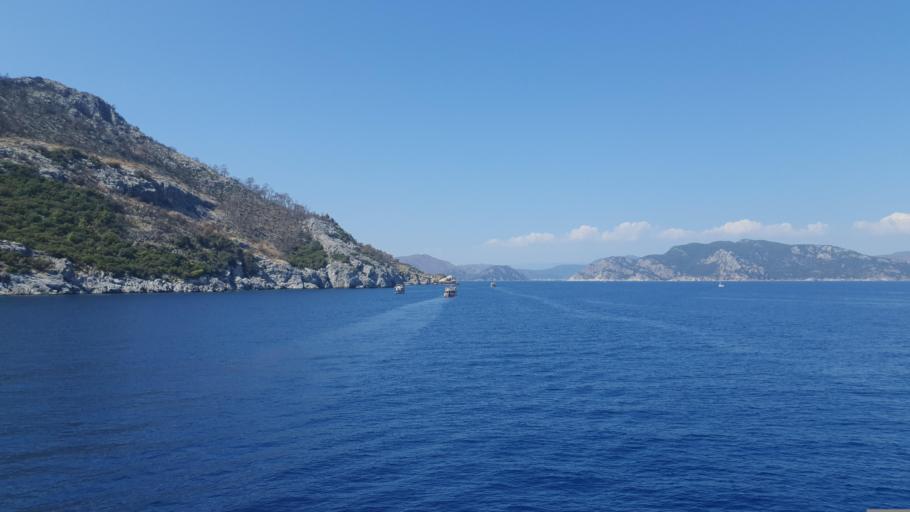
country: TR
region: Mugla
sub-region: Marmaris
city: Marmaris
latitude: 36.7384
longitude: 28.3003
